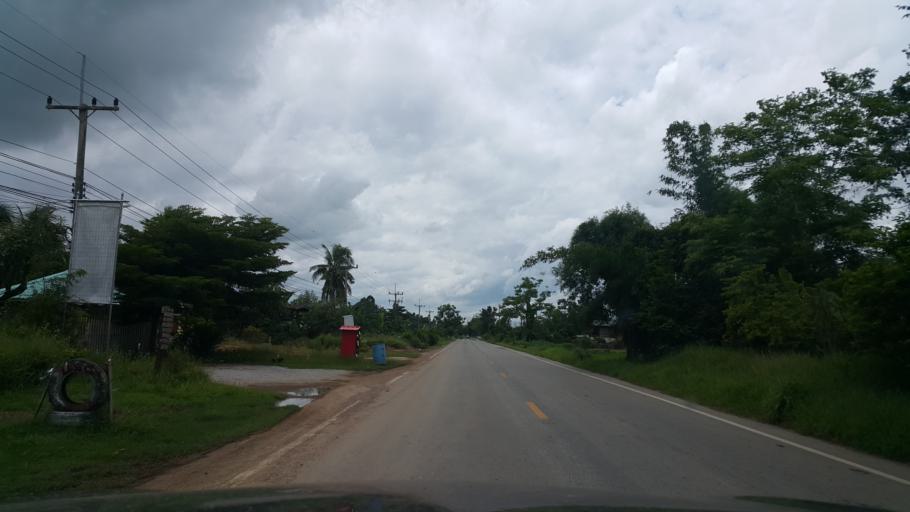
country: TH
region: Sukhothai
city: Kong Krailat
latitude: 16.9109
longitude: 99.8777
